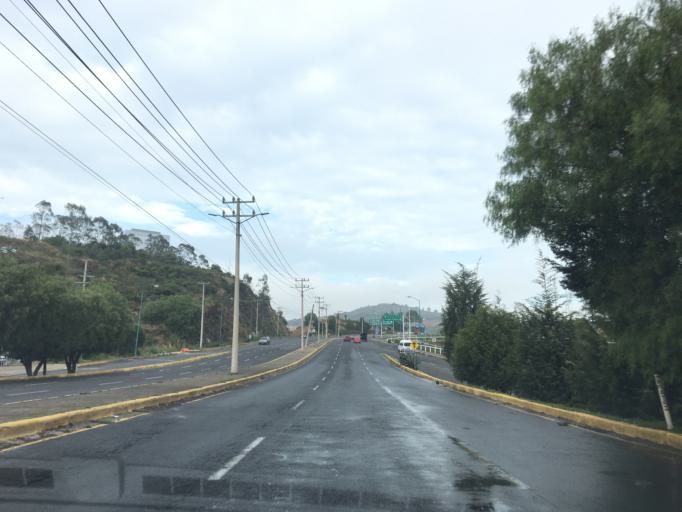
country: MX
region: Mexico
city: Ciudad Lopez Mateos
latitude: 19.5455
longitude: -99.2729
